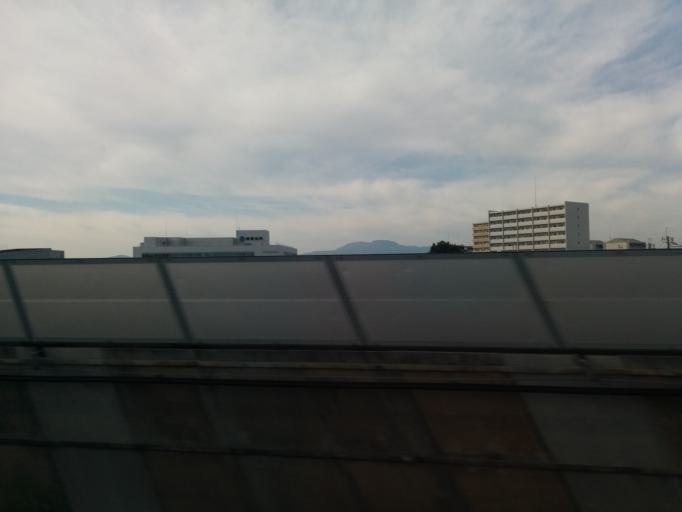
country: JP
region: Shiga Prefecture
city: Kusatsu
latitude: 34.9909
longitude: 135.9523
